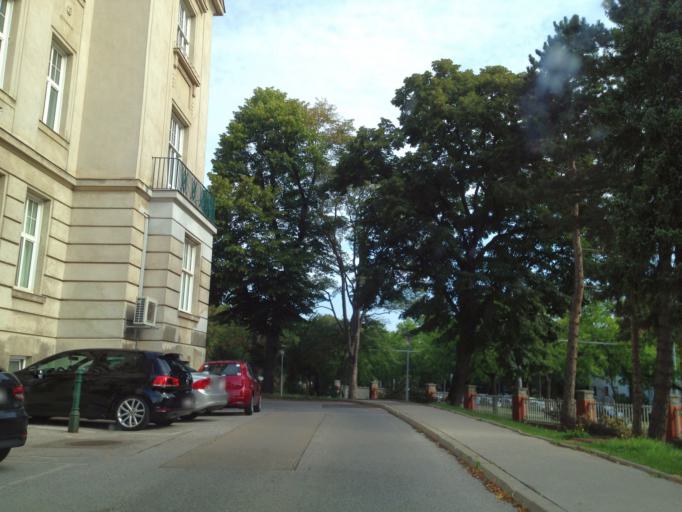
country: AT
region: Lower Austria
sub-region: Politischer Bezirk Modling
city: Perchtoldsdorf
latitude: 48.1694
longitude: 16.2782
